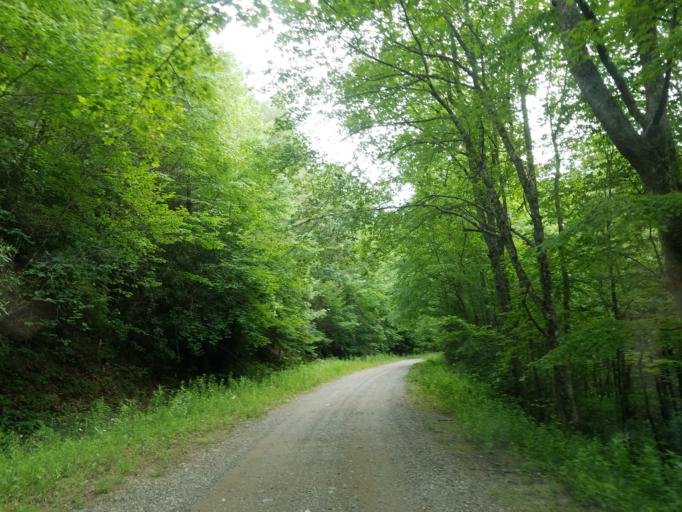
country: US
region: Georgia
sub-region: Union County
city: Blairsville
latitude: 34.7631
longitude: -84.0069
